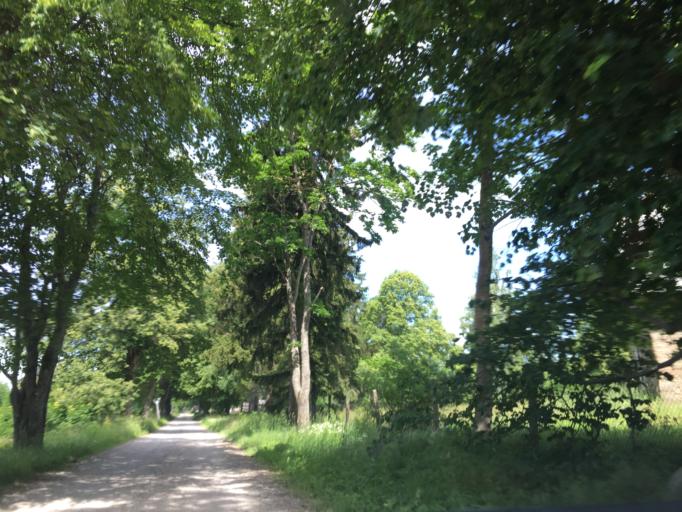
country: LV
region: Dundaga
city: Dundaga
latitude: 57.6251
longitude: 22.2936
